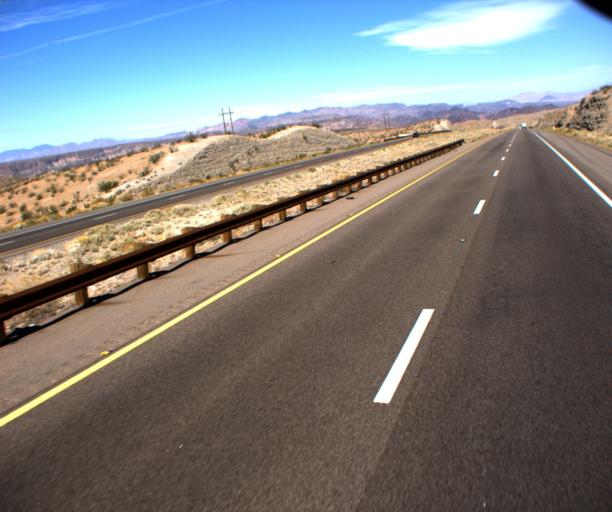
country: US
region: Nevada
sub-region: Clark County
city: Boulder City
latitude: 35.9587
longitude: -114.6603
